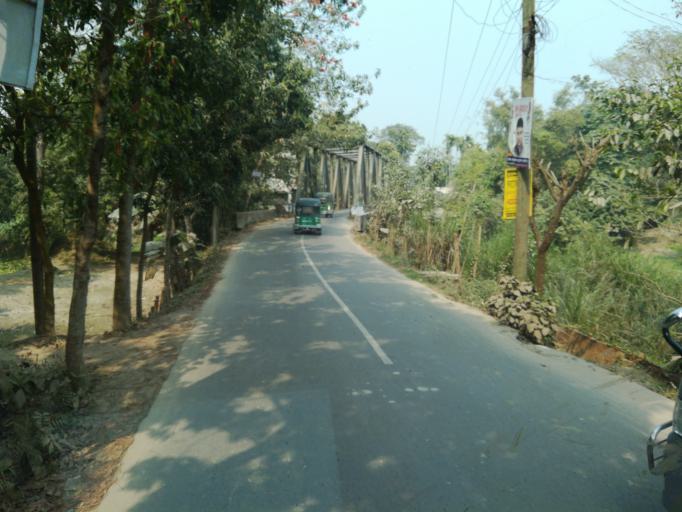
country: BD
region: Dhaka
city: Nagarpur
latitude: 24.0001
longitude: 89.8470
